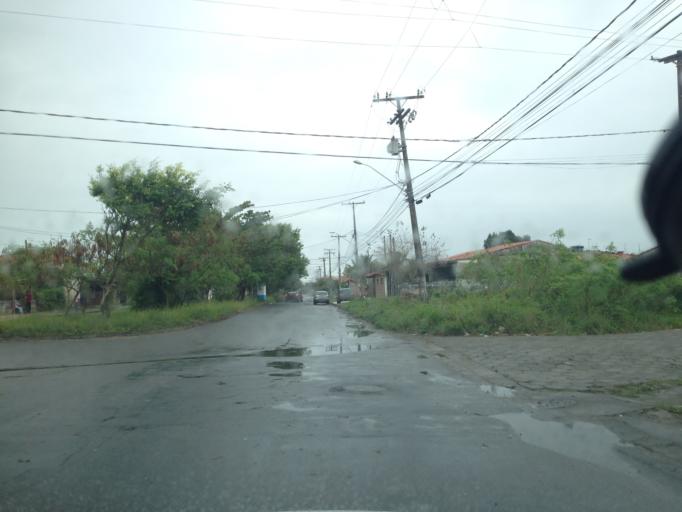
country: BR
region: Sao Paulo
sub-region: Itanhaem
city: Itanhaem
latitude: -24.2255
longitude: -46.8667
